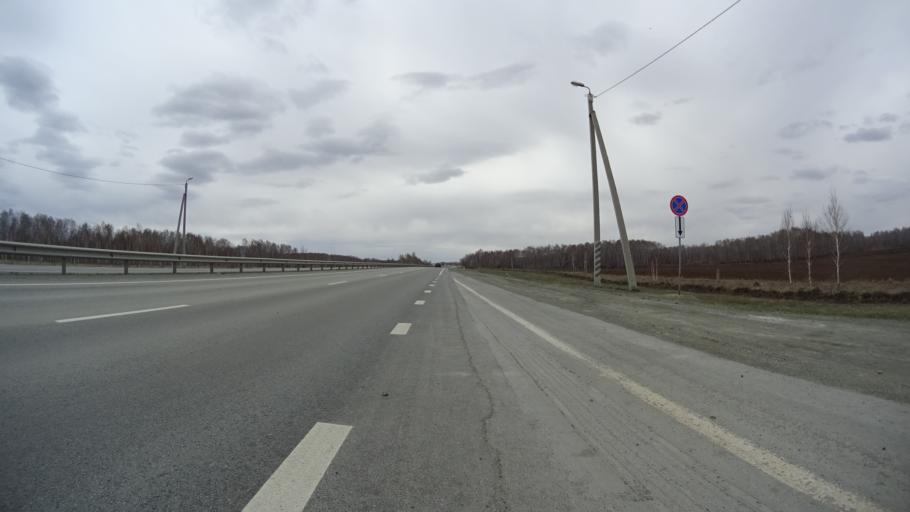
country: RU
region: Chelyabinsk
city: Yemanzhelinka
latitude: 54.8315
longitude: 61.3117
